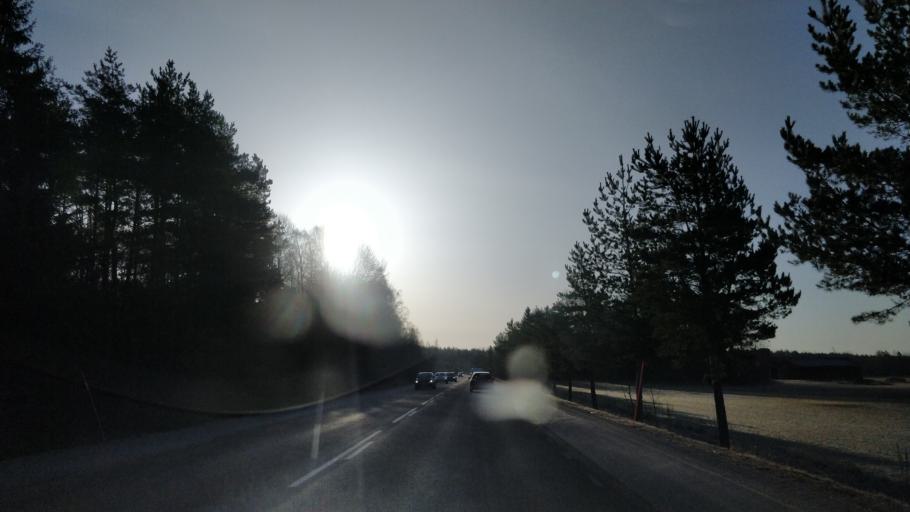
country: SE
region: Uppsala
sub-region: Enkopings Kommun
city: Enkoping
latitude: 59.6465
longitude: 17.1327
